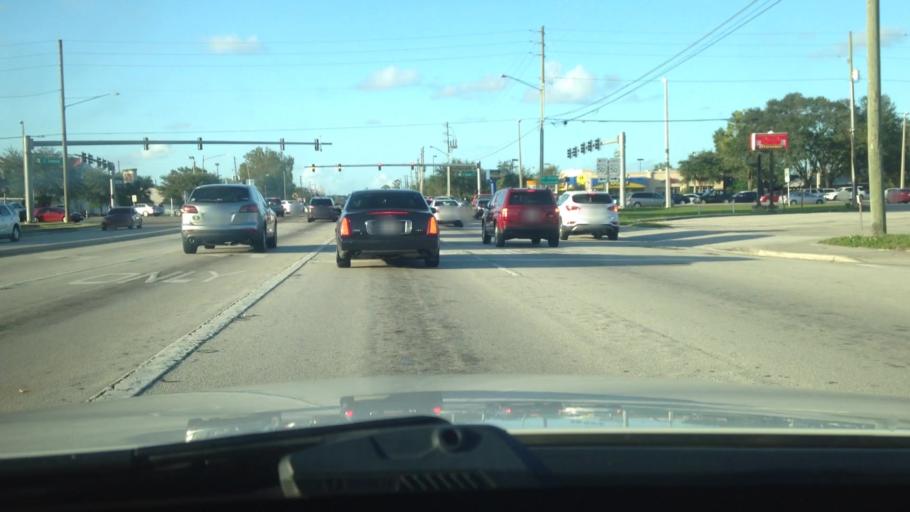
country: US
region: Florida
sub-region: Orange County
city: Union Park
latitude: 28.5673
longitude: -81.2860
